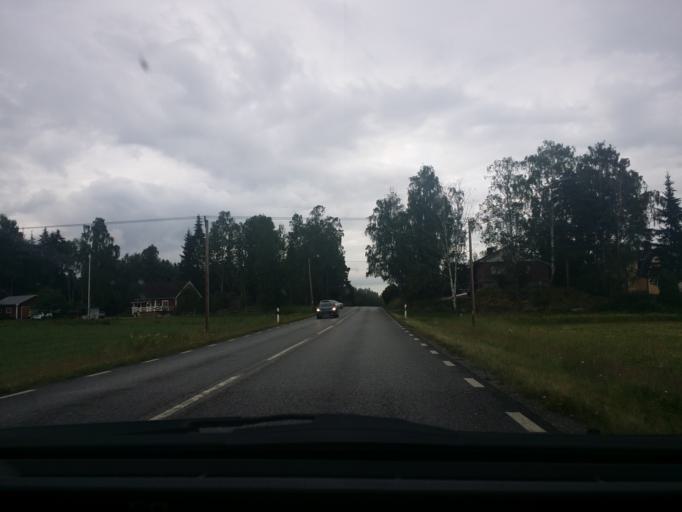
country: SE
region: OErebro
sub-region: Lindesbergs Kommun
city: Frovi
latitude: 59.4610
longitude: 15.3212
